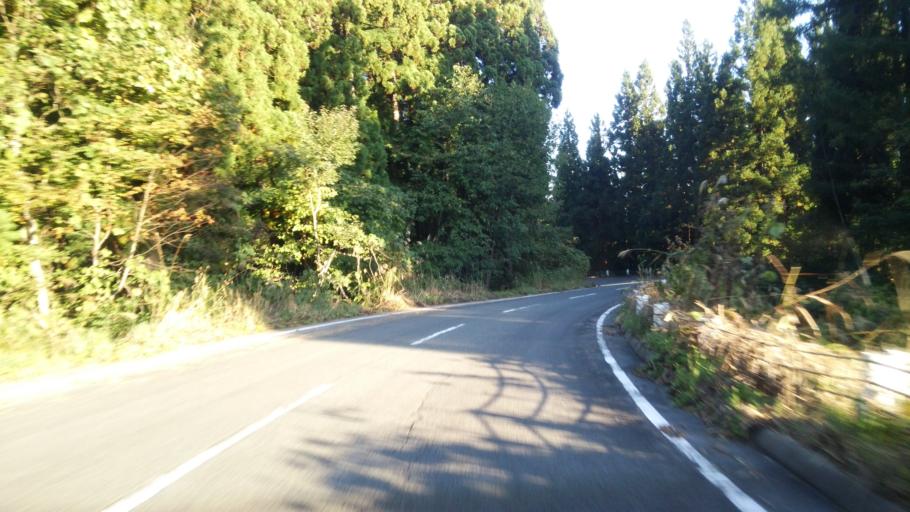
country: JP
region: Fukushima
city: Kitakata
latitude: 37.4248
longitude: 139.7836
